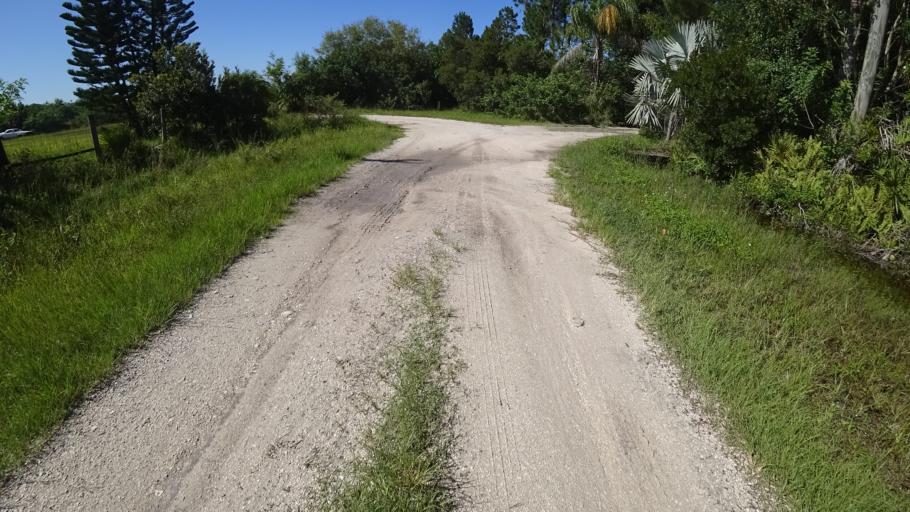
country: US
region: Florida
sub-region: Sarasota County
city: Fruitville
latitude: 27.3999
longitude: -82.2958
